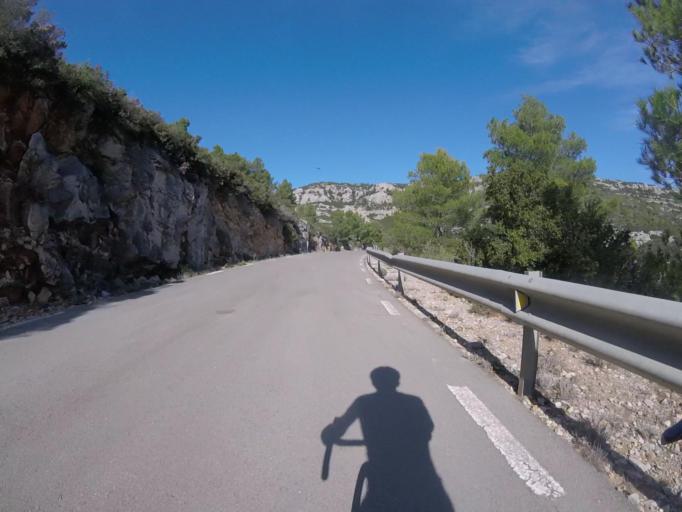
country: ES
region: Valencia
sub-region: Provincia de Castello
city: Sarratella
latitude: 40.2718
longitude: 0.0492
